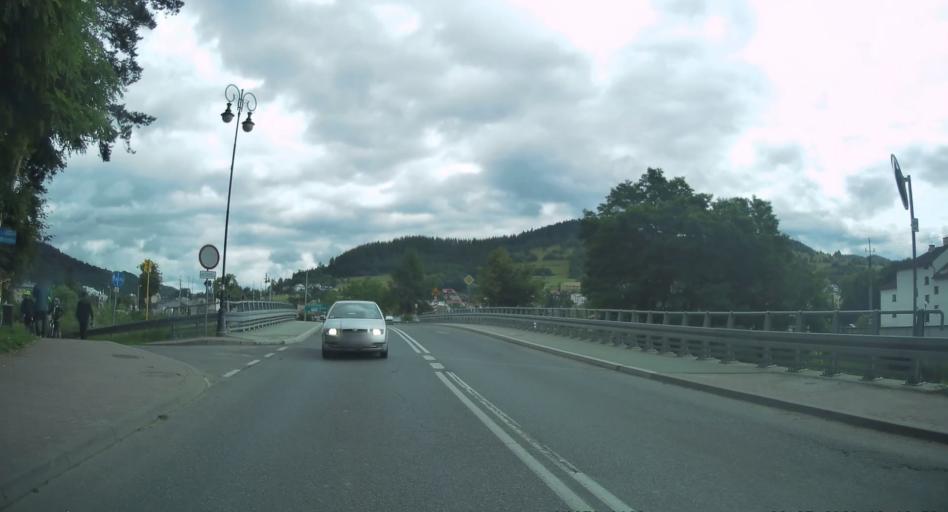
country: PL
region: Lesser Poland Voivodeship
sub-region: Powiat nowosadecki
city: Muszyna
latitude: 49.3531
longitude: 20.8910
